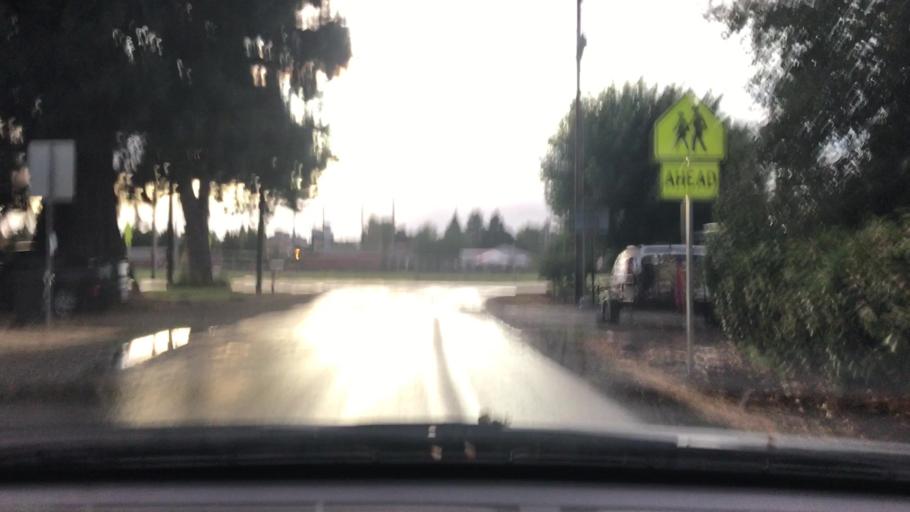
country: US
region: Oregon
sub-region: Yamhill County
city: McMinnville
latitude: 45.1981
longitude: -123.1947
